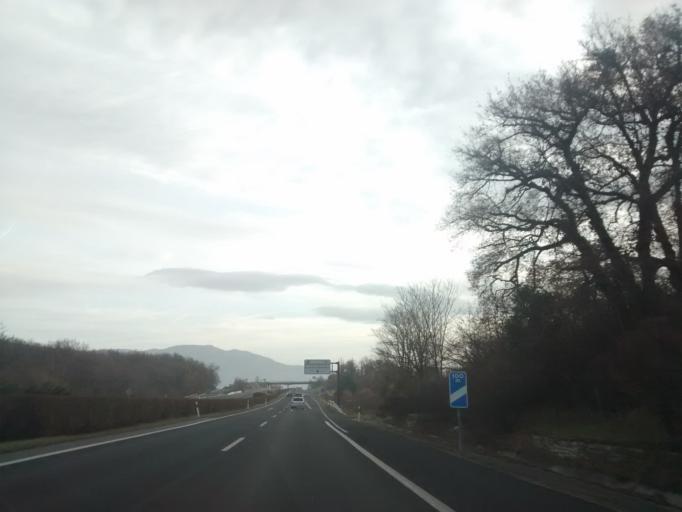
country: ES
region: Navarre
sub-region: Provincia de Navarra
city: Bakaiku
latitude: 42.8950
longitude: -2.0852
